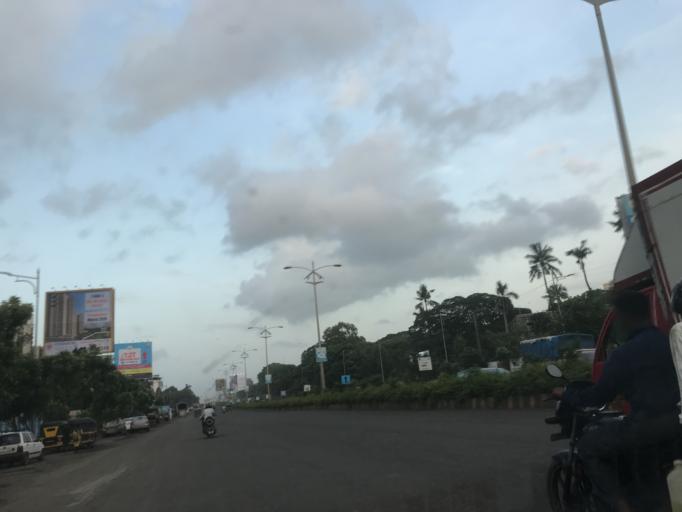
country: IN
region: Maharashtra
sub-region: Thane
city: Thane
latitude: 19.2191
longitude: 72.9848
